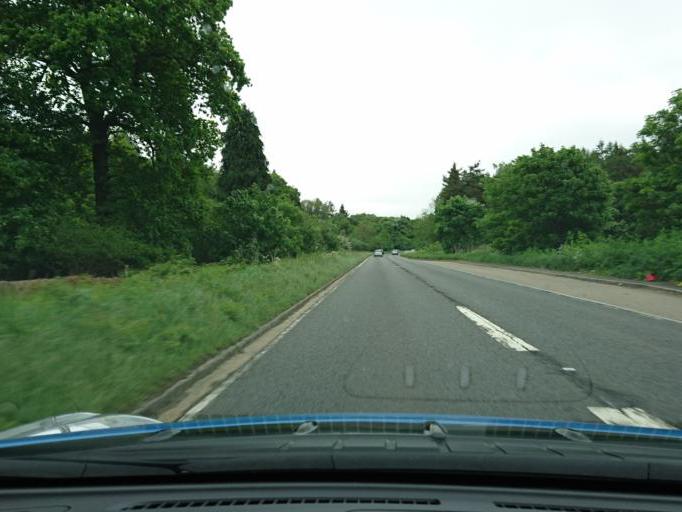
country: GB
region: England
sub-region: Oxfordshire
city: Frilford
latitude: 51.6935
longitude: -1.3657
